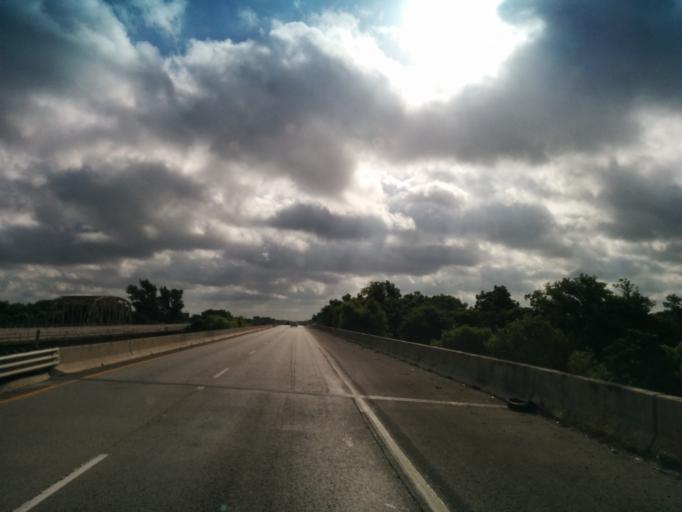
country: US
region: Texas
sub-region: Guadalupe County
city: Cibolo
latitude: 29.5005
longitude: -98.1875
